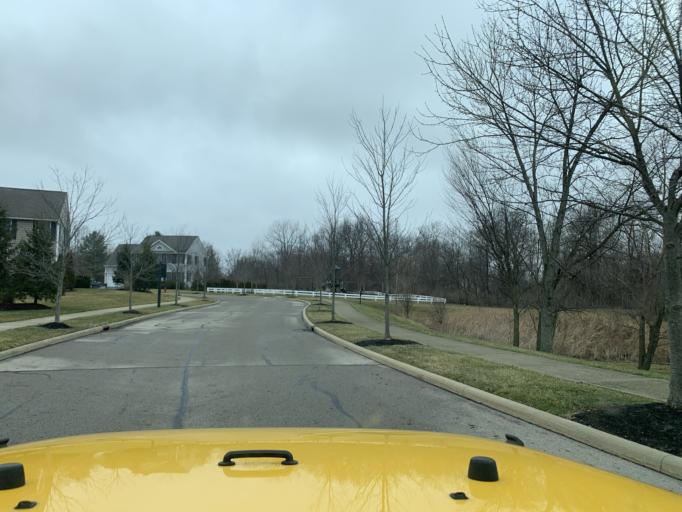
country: US
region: Ohio
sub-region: Franklin County
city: New Albany
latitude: 40.0951
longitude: -82.8100
